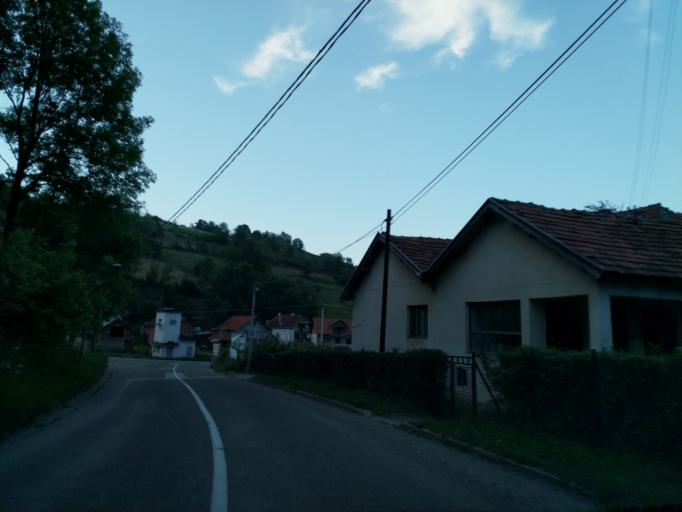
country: XK
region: Mitrovica
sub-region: Komuna e Leposaviqit
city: Leposaviq
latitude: 43.3001
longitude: 20.8851
